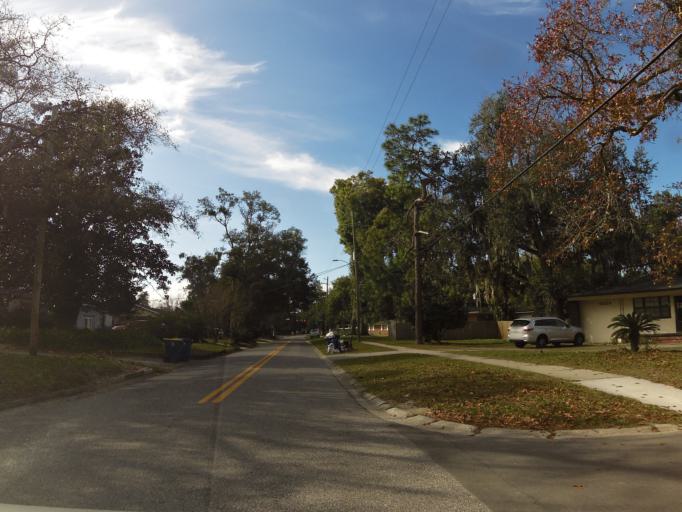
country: US
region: Florida
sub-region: Duval County
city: Jacksonville
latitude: 30.3378
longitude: -81.5953
